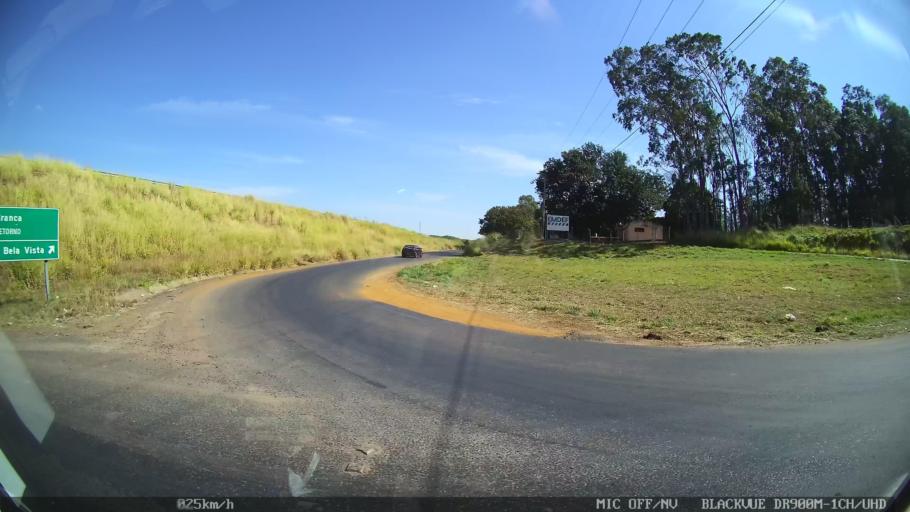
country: BR
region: Sao Paulo
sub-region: Franca
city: Franca
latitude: -20.5462
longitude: -47.4641
